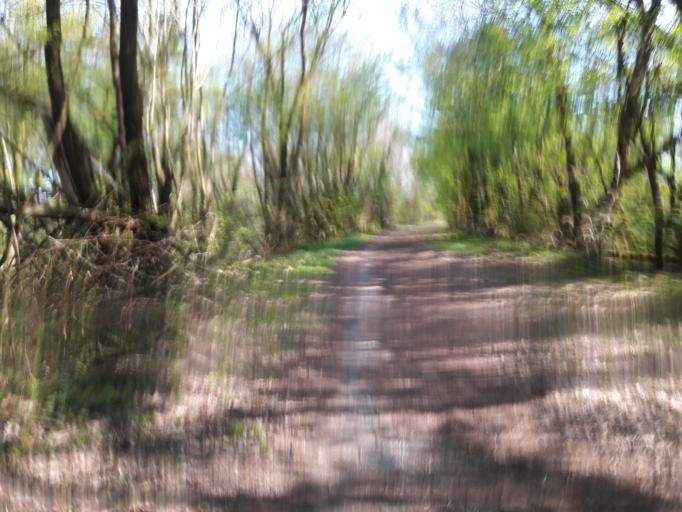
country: FR
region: Nord-Pas-de-Calais
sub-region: Departement du Nord
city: Sains-du-Nord
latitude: 50.1252
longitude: 4.0669
